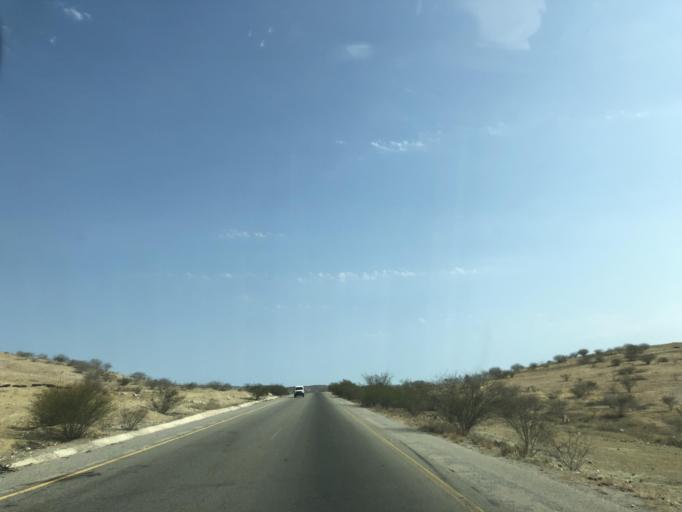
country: AO
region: Benguela
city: Benguela
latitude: -12.7337
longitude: 13.3490
